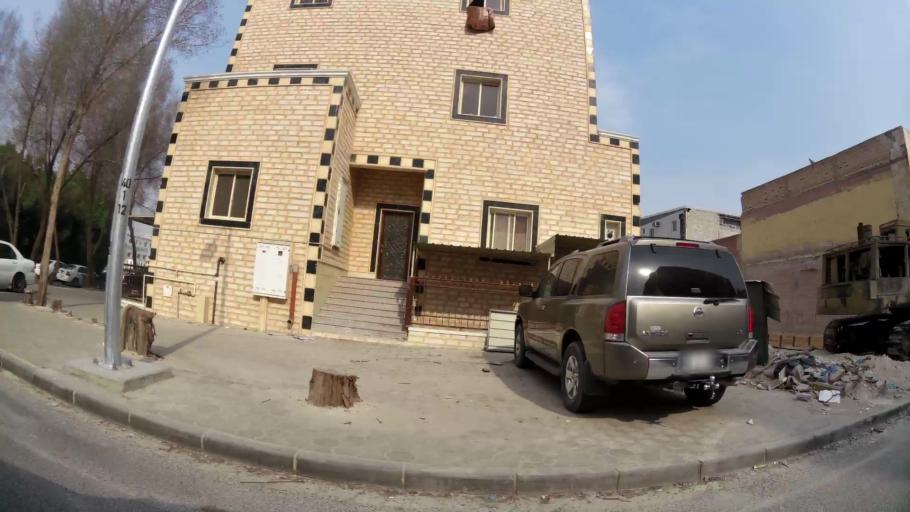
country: KW
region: Al Farwaniyah
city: Al Farwaniyah
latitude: 29.2802
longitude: 47.9529
